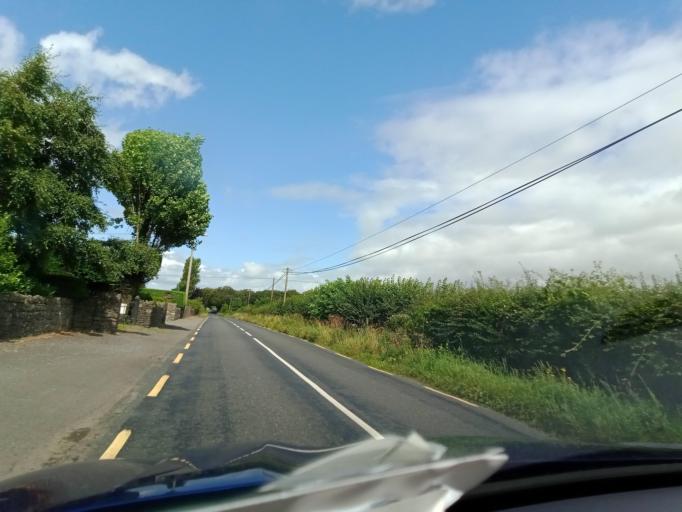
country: IE
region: Leinster
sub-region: Laois
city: Abbeyleix
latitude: 52.9335
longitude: -7.3226
